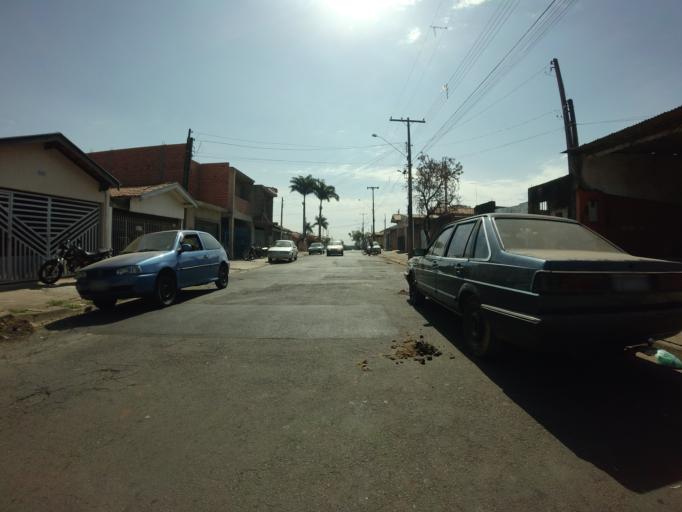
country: BR
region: Sao Paulo
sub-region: Piracicaba
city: Piracicaba
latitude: -22.7594
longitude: -47.5996
